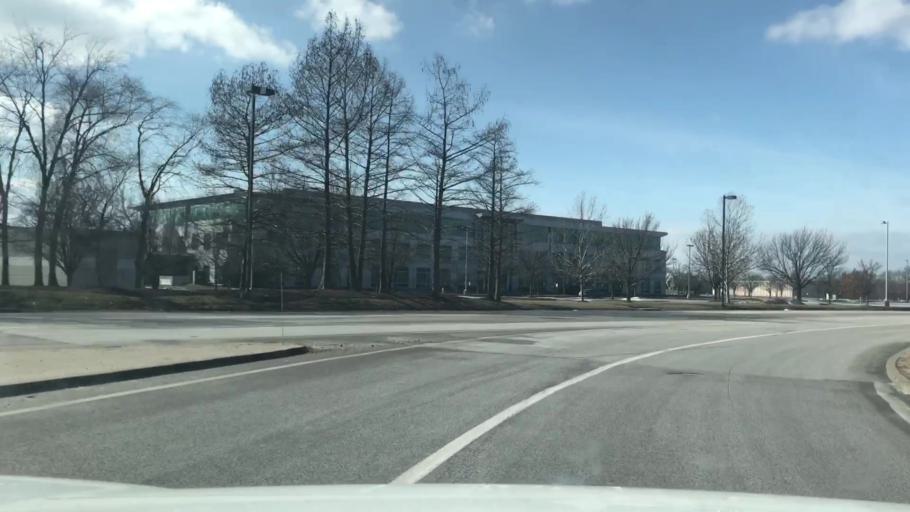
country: US
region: Missouri
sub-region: Saint Charles County
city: Saint Charles
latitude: 38.7493
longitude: -90.4630
